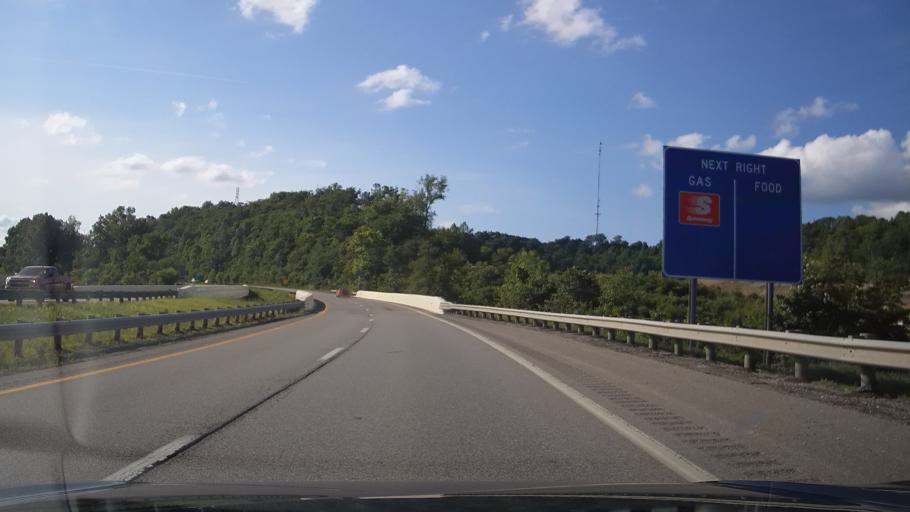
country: US
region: Ohio
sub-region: Lawrence County
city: Coal Grove
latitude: 38.5150
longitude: -82.6521
